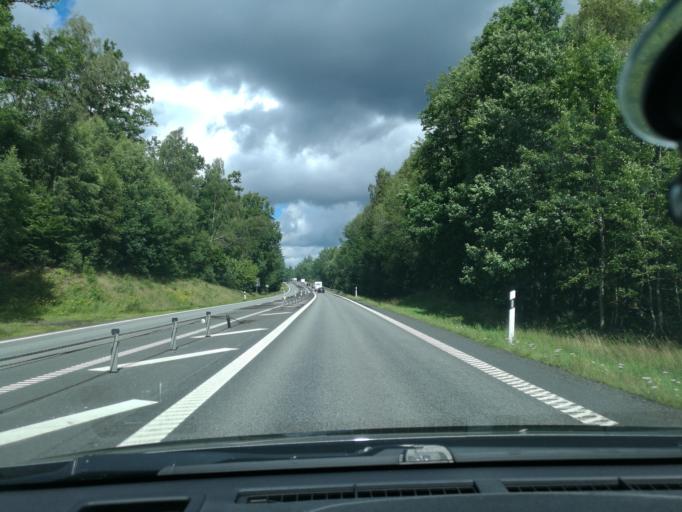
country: SE
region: Skane
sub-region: Osby Kommun
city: Osby
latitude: 56.3779
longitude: 14.0359
